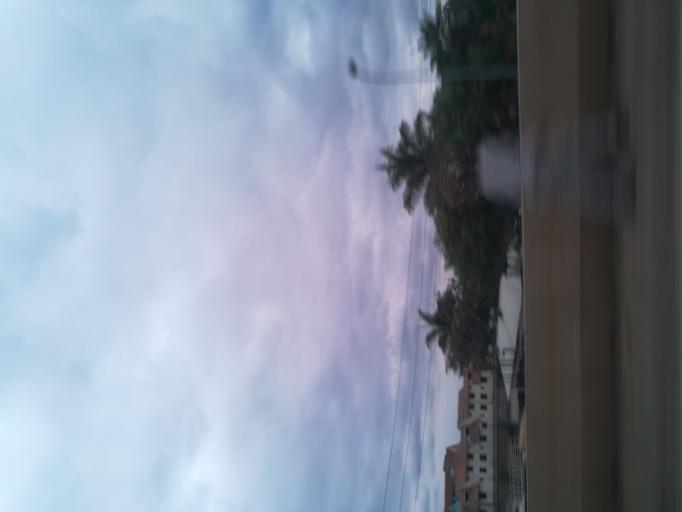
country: KE
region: Nairobi Area
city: Pumwani
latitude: -1.3233
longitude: 36.8481
